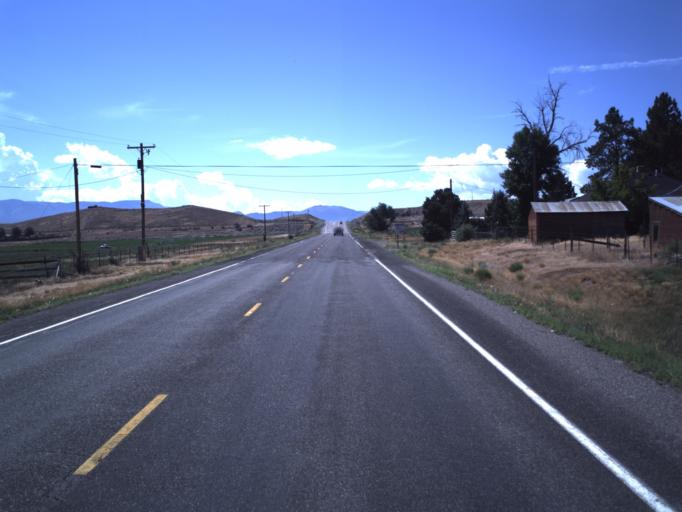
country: US
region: Utah
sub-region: Sevier County
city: Monroe
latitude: 38.4672
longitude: -112.2348
